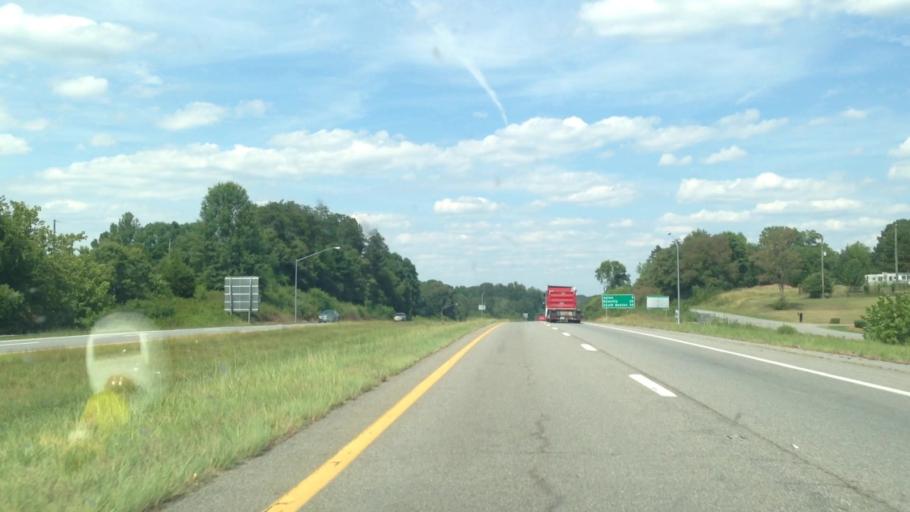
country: US
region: Virginia
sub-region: Henry County
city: Chatmoss
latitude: 36.6279
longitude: -79.8466
